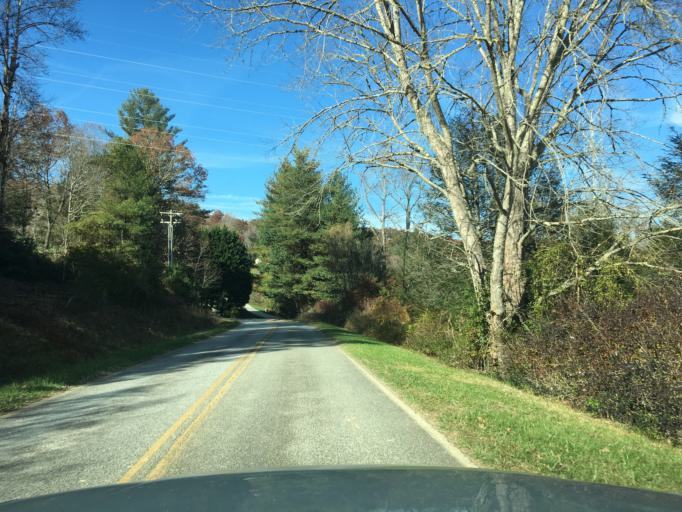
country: US
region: North Carolina
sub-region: Henderson County
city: Etowah
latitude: 35.3301
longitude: -82.6151
